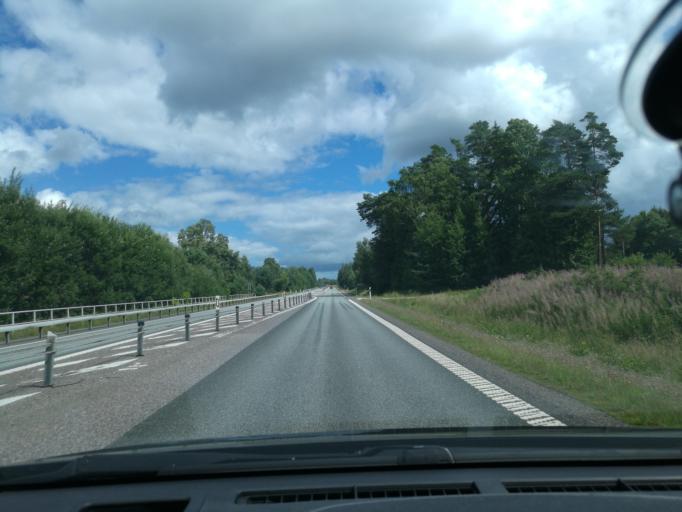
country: SE
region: Skane
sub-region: Hassleholms Kommun
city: Hastveda
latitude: 56.2477
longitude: 13.9185
